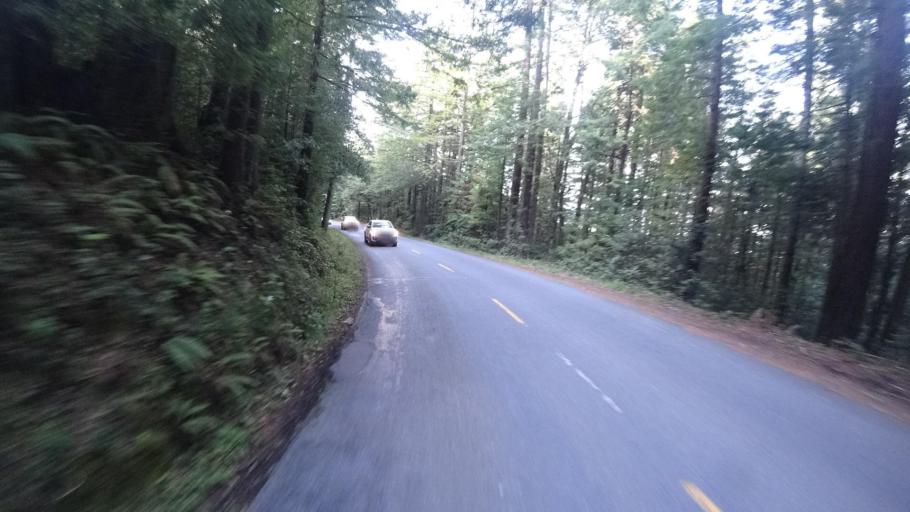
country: US
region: California
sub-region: Humboldt County
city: Bayside
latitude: 40.7626
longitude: -124.0006
